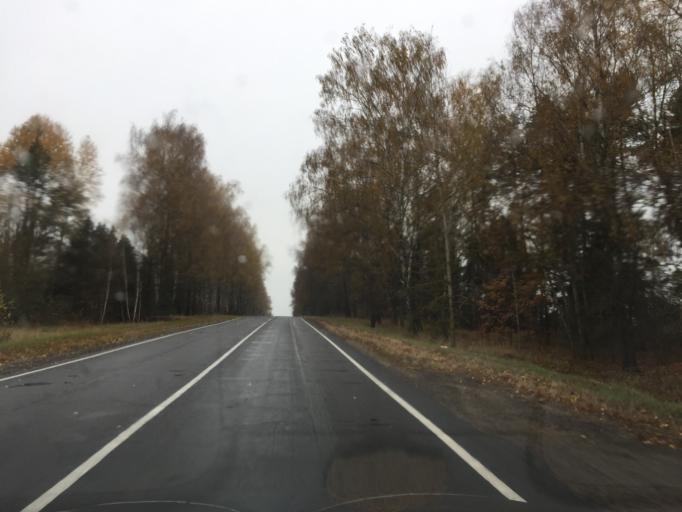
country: BY
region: Gomel
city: Karma
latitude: 53.3361
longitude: 30.7930
